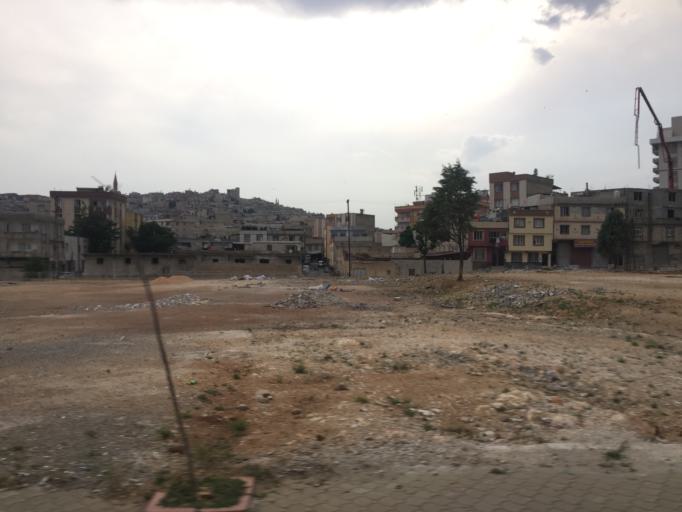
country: TR
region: Gaziantep
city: Gaziantep
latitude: 37.0728
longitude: 37.4130
